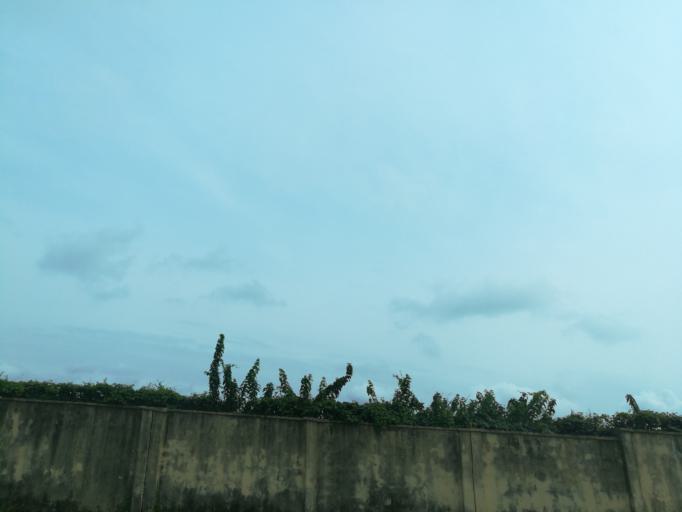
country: NG
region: Lagos
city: Oshodi
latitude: 6.5658
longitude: 3.3274
